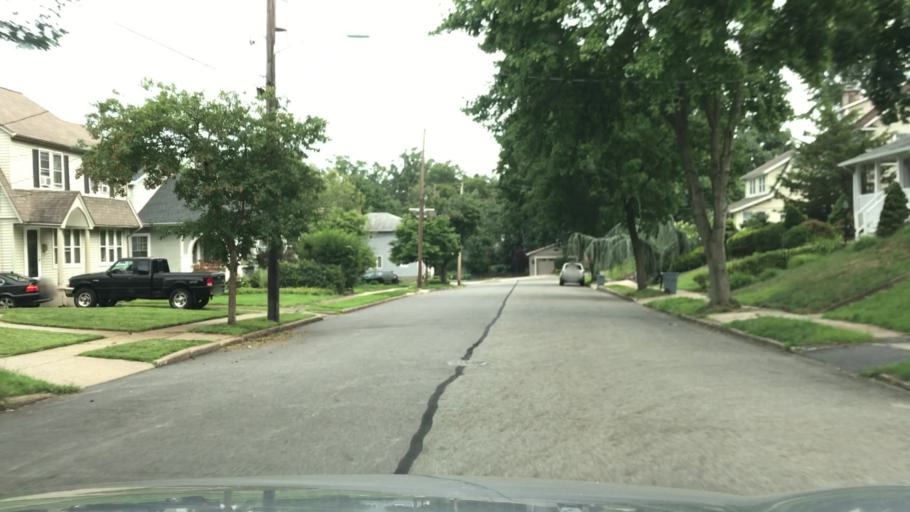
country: US
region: New Jersey
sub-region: Bergen County
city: Westwood
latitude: 40.9884
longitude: -74.0255
